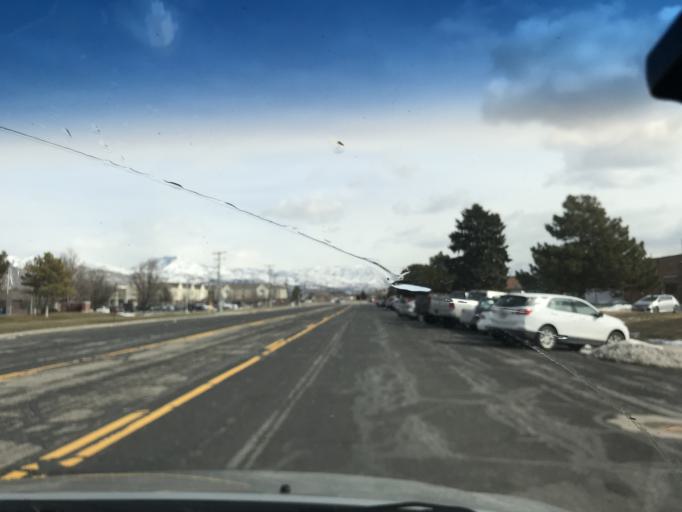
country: US
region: Utah
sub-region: Salt Lake County
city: Salt Lake City
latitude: 40.7714
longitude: -111.9567
